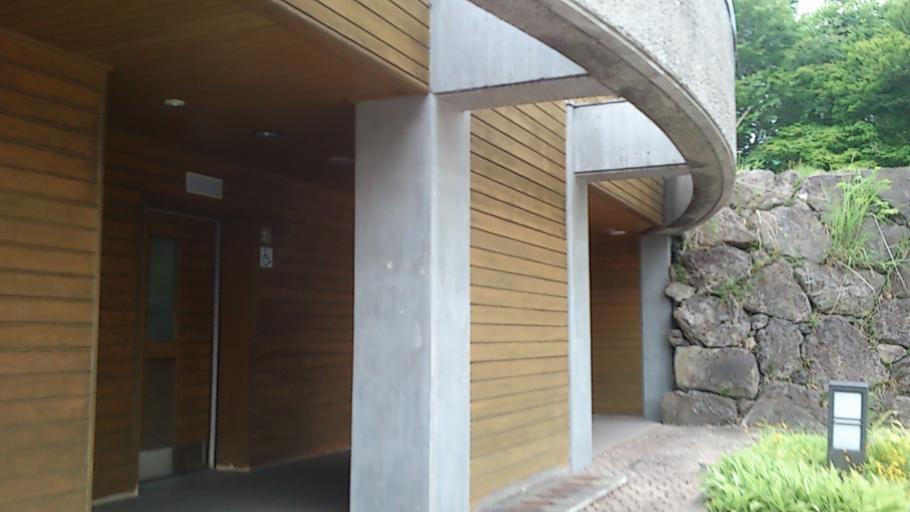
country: JP
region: Aomori
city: Hirosaki
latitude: 40.5783
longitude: 140.2995
